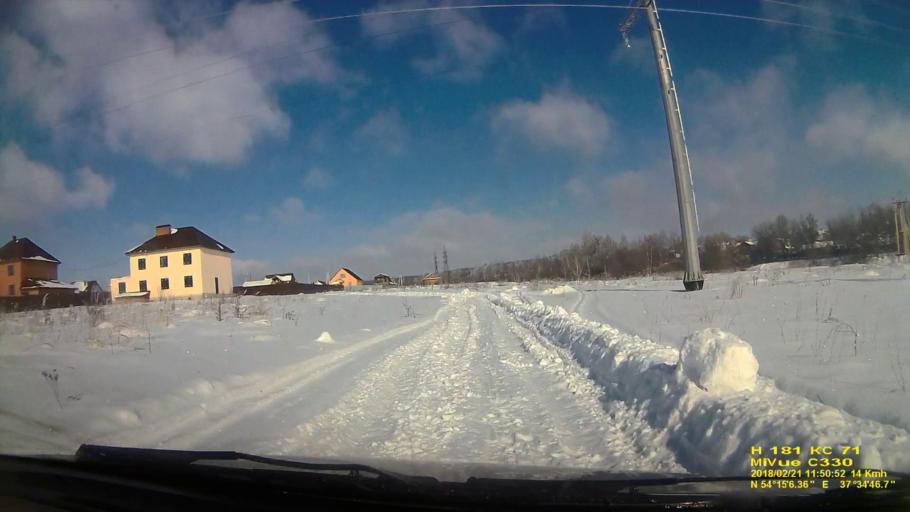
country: RU
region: Tula
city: Gorelki
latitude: 54.2518
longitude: 37.5796
